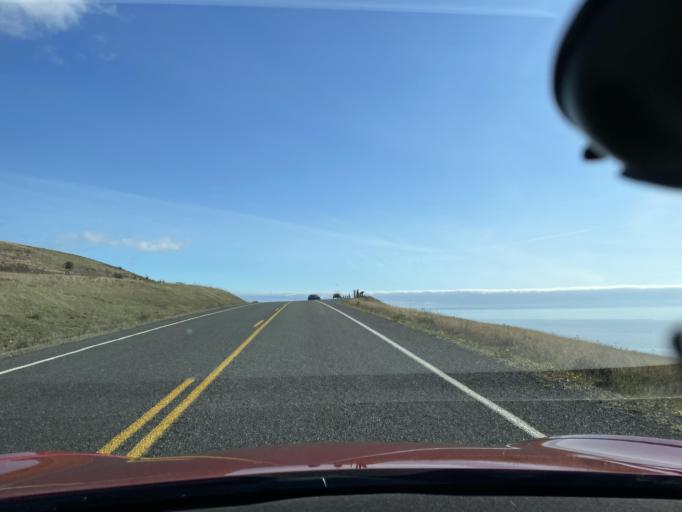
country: US
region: Washington
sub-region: San Juan County
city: Friday Harbor
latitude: 48.4583
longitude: -122.9934
